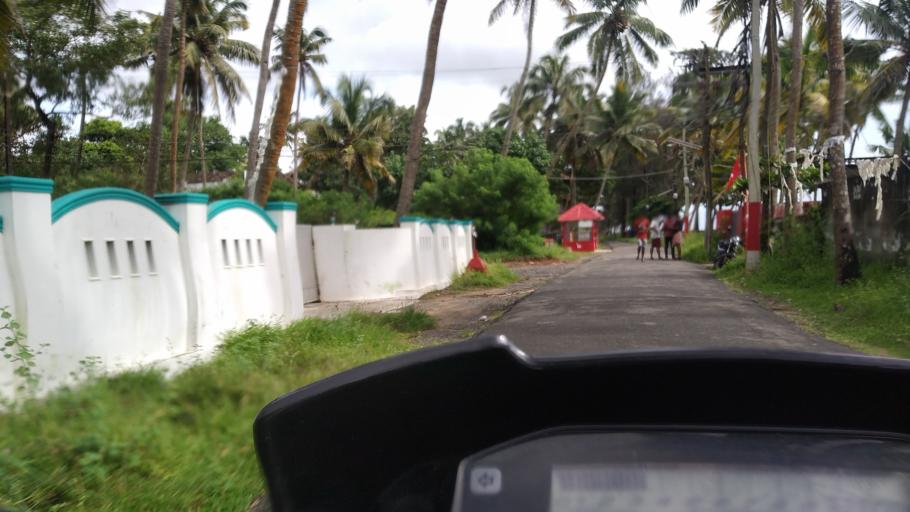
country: IN
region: Kerala
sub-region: Thrissur District
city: Kodungallur
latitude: 10.1600
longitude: 76.1721
